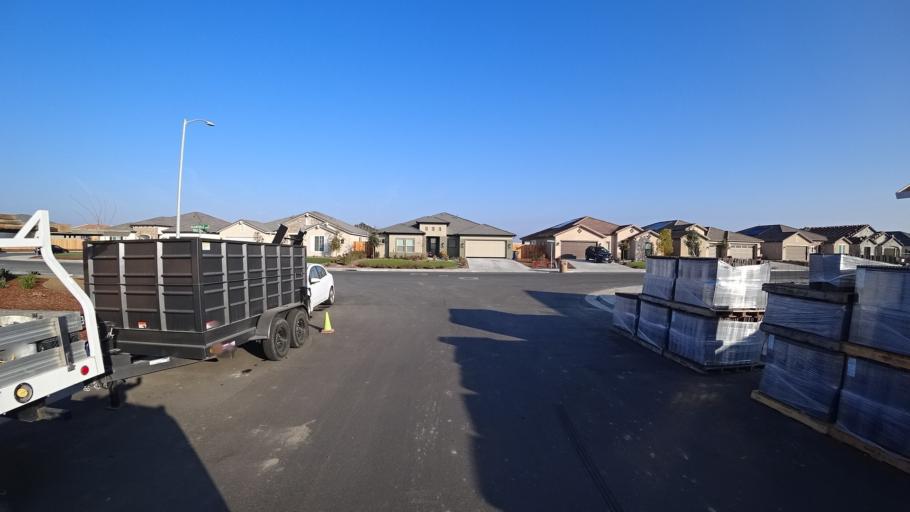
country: US
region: California
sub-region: Kern County
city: Greenacres
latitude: 35.2936
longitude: -119.1125
